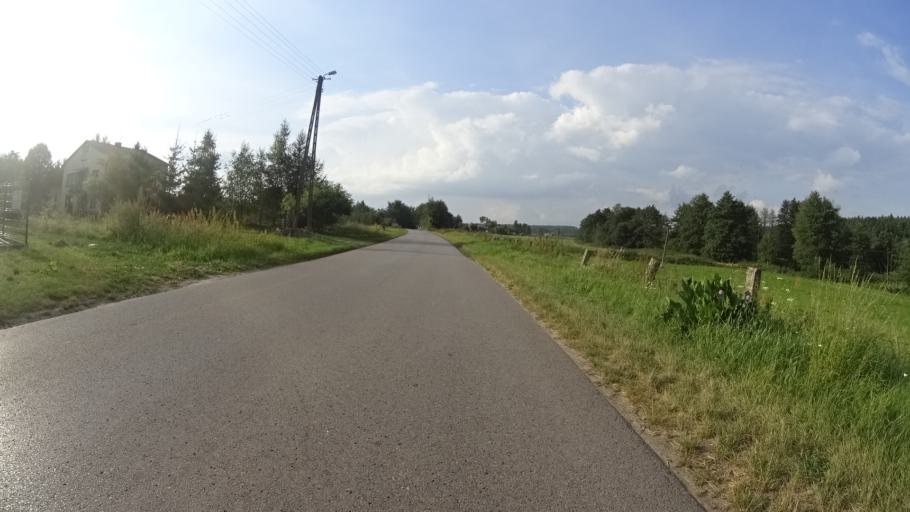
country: PL
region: Masovian Voivodeship
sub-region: Powiat grojecki
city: Mogielnica
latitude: 51.6800
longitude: 20.7333
